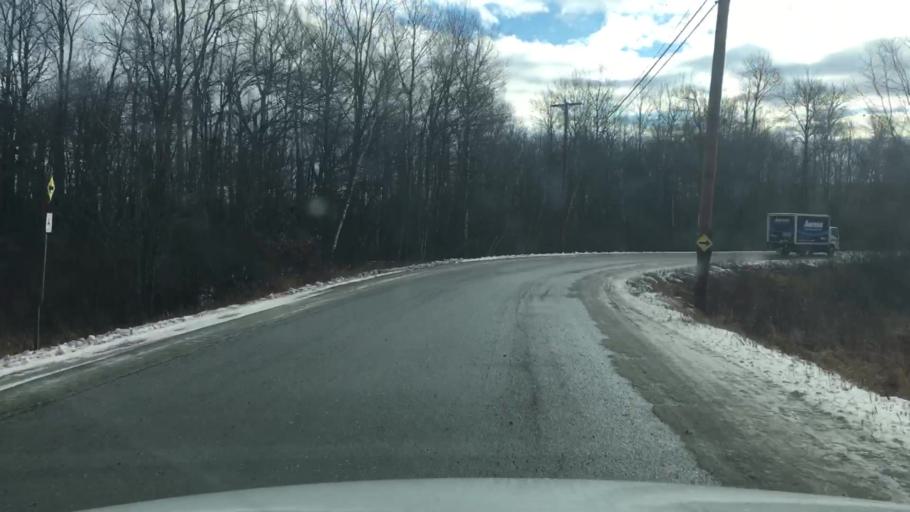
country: US
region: Maine
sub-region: Penobscot County
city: Brewer
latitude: 44.7292
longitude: -68.7559
